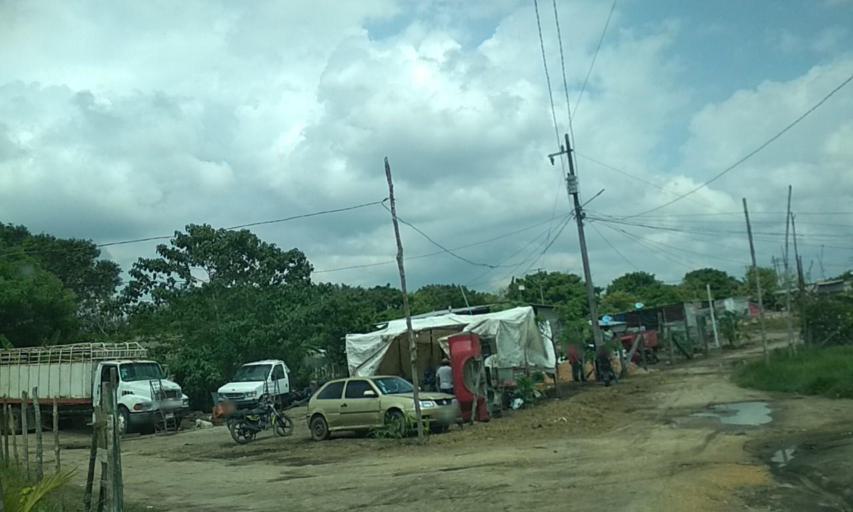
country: MX
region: Veracruz
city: Las Choapas
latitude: 17.8893
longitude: -94.1130
